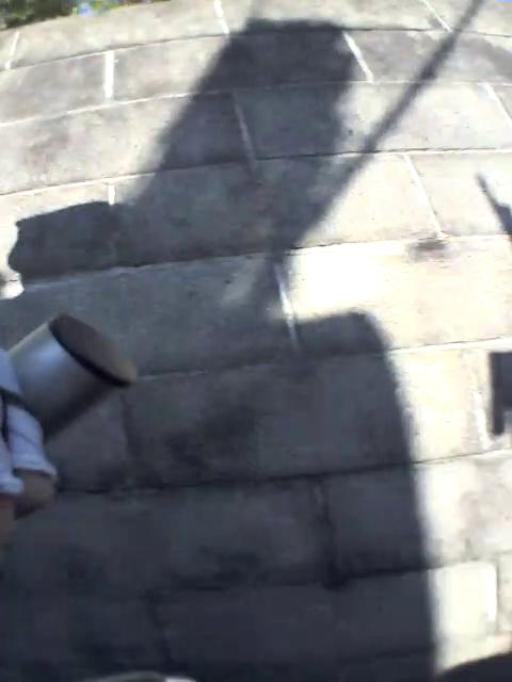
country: JP
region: Yamaguchi
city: Nagato
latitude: 34.3905
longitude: 131.1991
